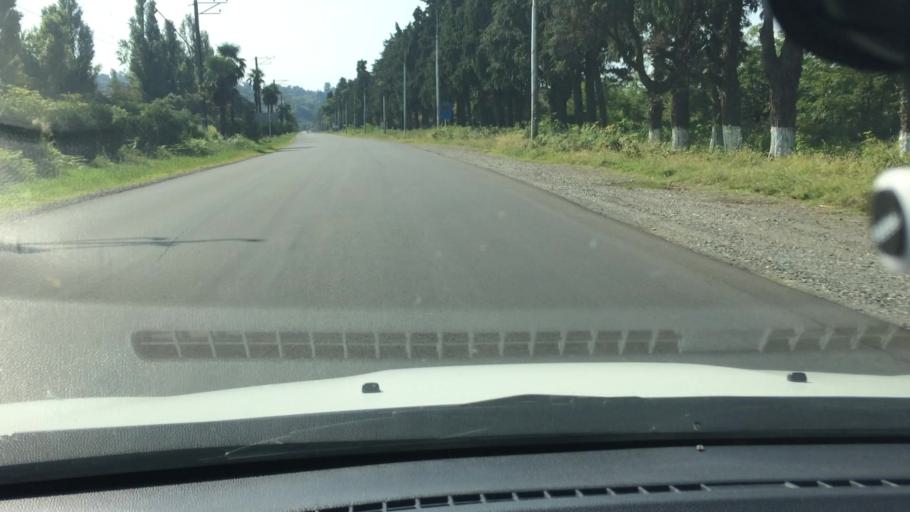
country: GE
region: Ajaria
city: Kobuleti
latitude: 41.7894
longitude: 41.7674
